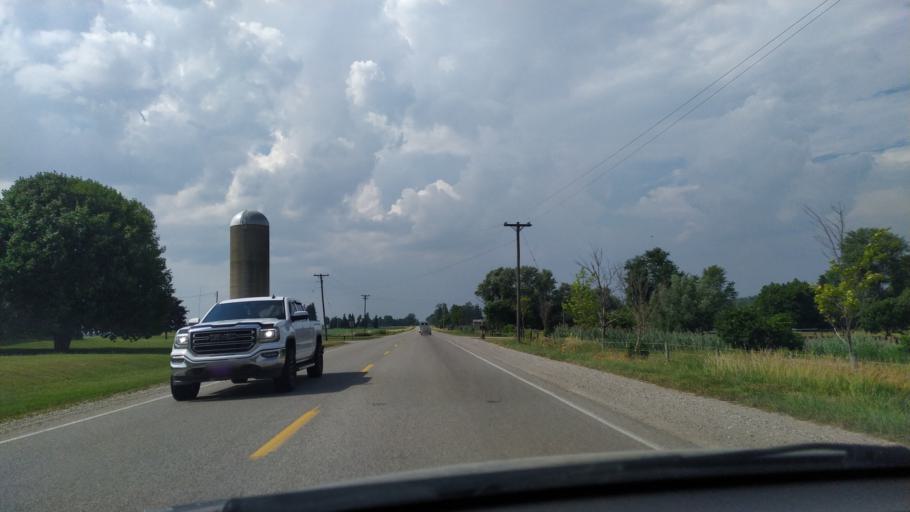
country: CA
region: Ontario
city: Dorchester
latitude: 43.0281
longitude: -81.1195
